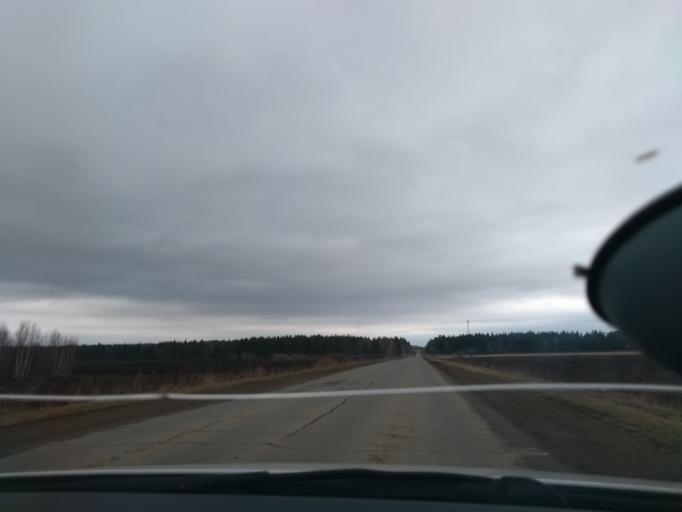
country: RU
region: Perm
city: Kungur
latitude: 57.3915
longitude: 56.8684
